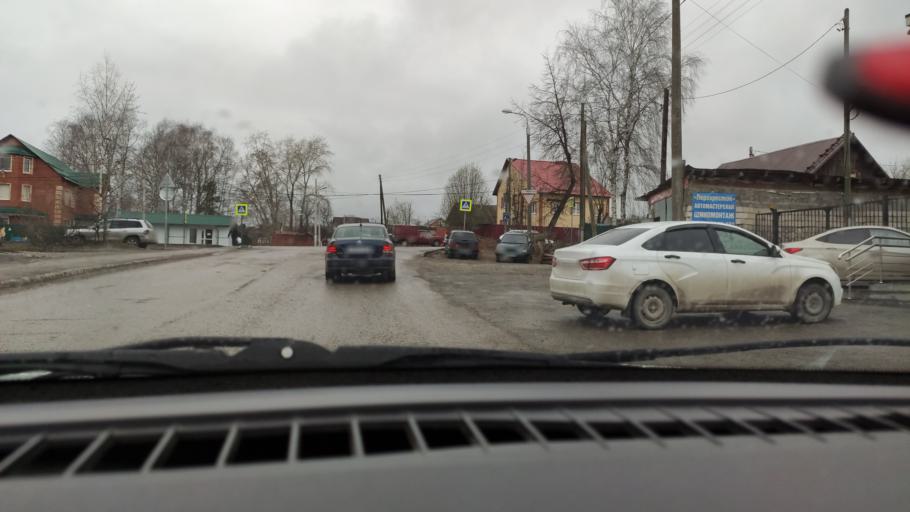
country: RU
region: Perm
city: Perm
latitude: 58.1066
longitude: 56.2968
